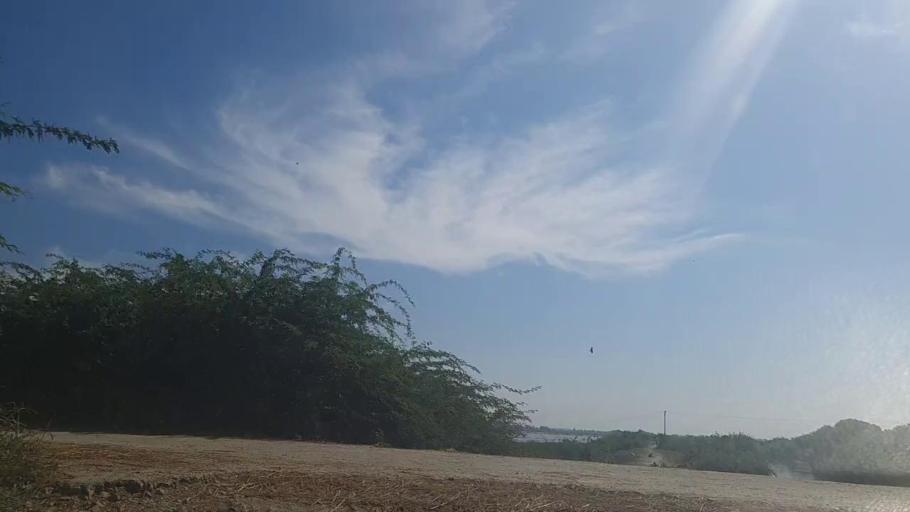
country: PK
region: Sindh
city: Mirpur Batoro
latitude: 24.6534
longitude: 68.2034
